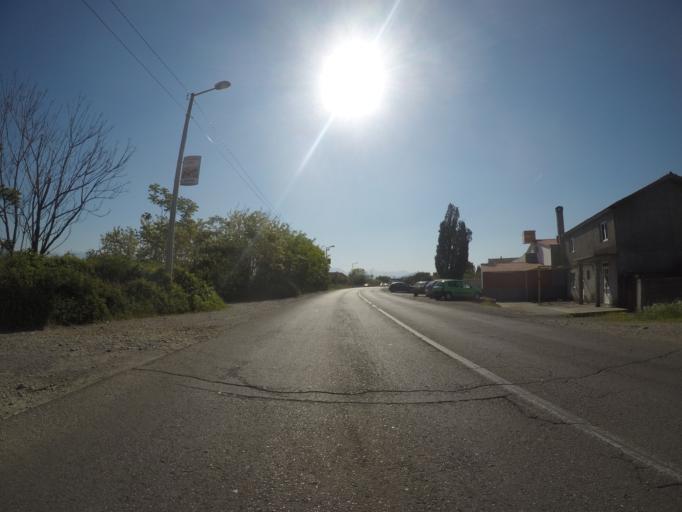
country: ME
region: Podgorica
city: Podgorica
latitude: 42.4428
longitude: 19.2141
